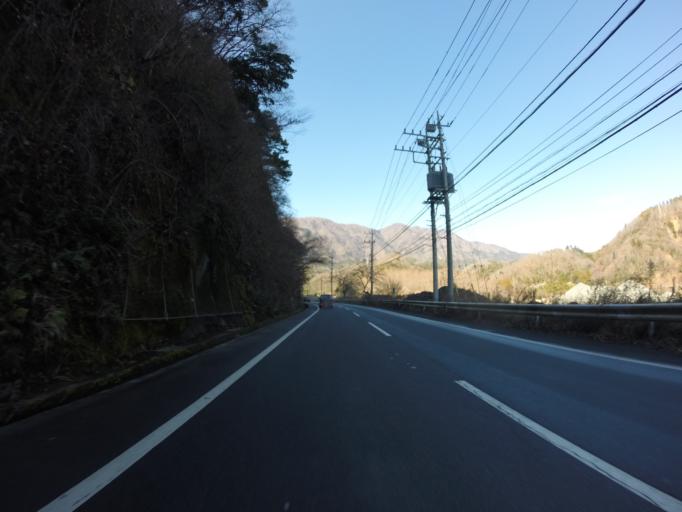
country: JP
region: Yamanashi
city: Ryuo
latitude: 35.4341
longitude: 138.4183
